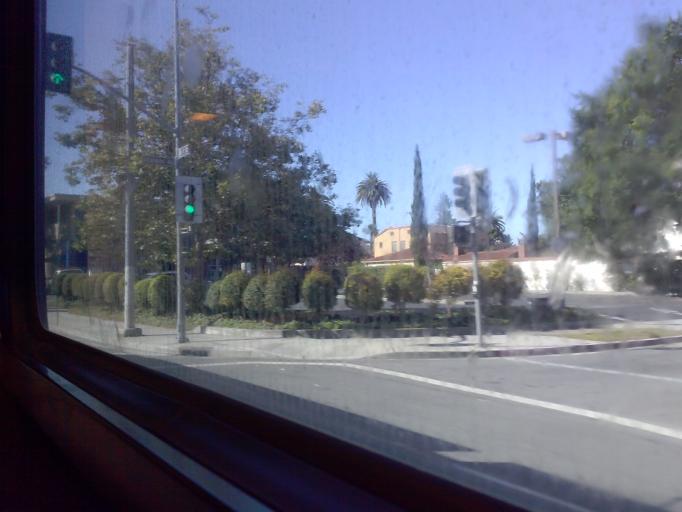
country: US
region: California
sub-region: Santa Clara County
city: San Jose
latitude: 37.3460
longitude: -121.8980
